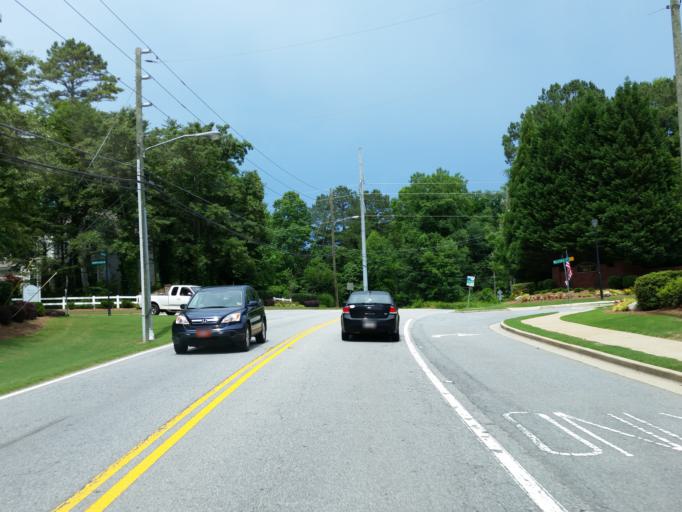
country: US
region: Georgia
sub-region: Fulton County
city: Alpharetta
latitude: 34.0785
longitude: -84.3435
